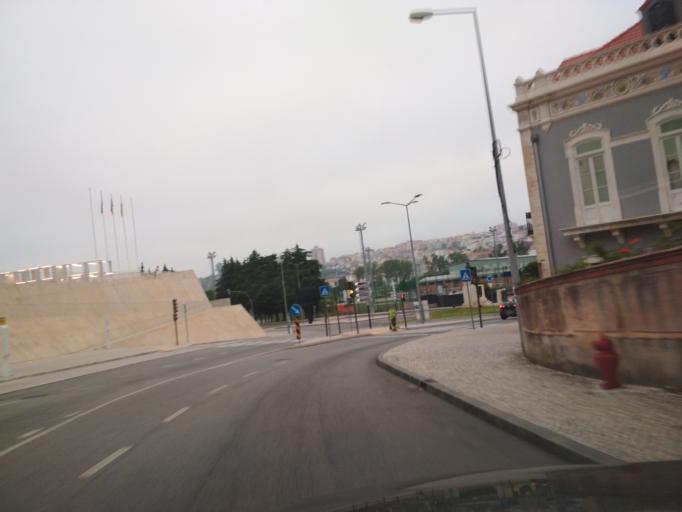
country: PT
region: Coimbra
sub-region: Coimbra
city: Coimbra
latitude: 40.2028
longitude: -8.4355
